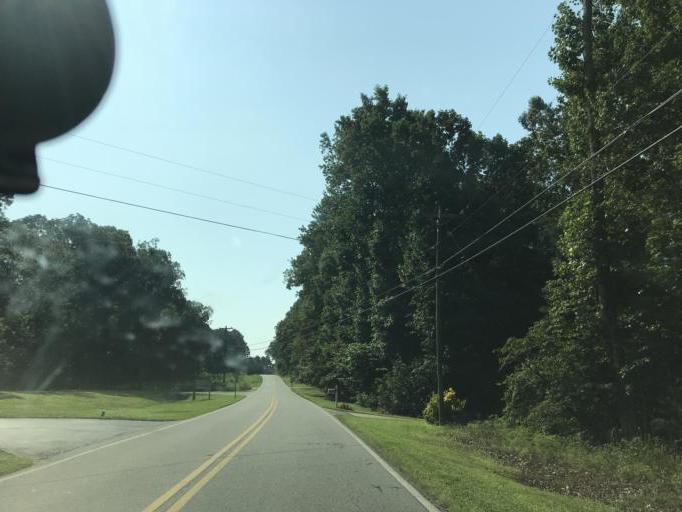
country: US
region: Georgia
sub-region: Forsyth County
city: Cumming
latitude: 34.2376
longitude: -84.1083
